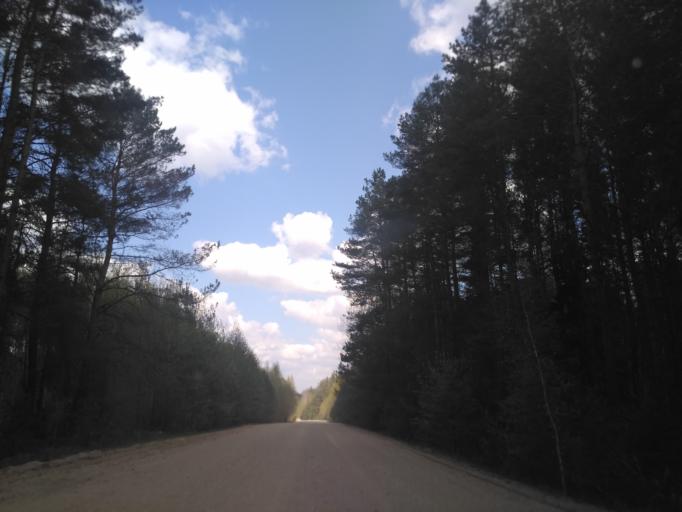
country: BY
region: Minsk
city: Radashkovichy
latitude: 54.2386
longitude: 27.2869
